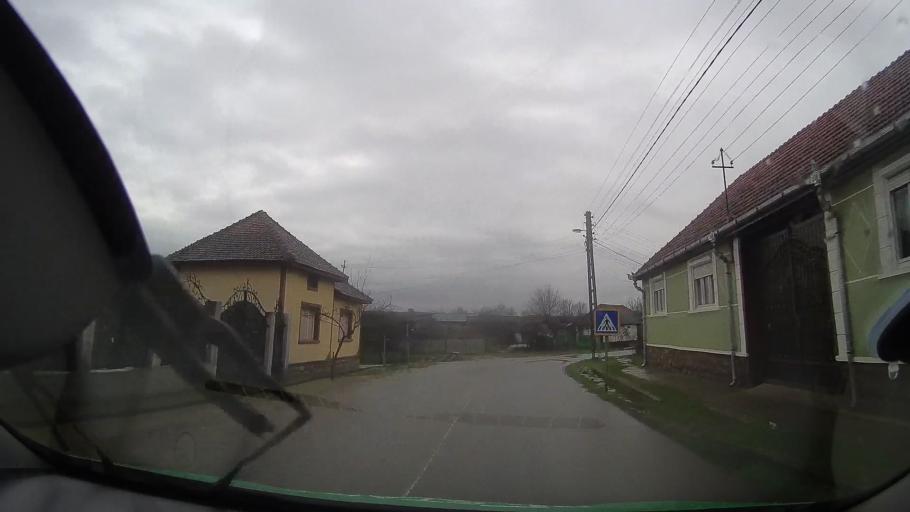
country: RO
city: Capalna
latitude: 46.7066
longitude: 22.0523
